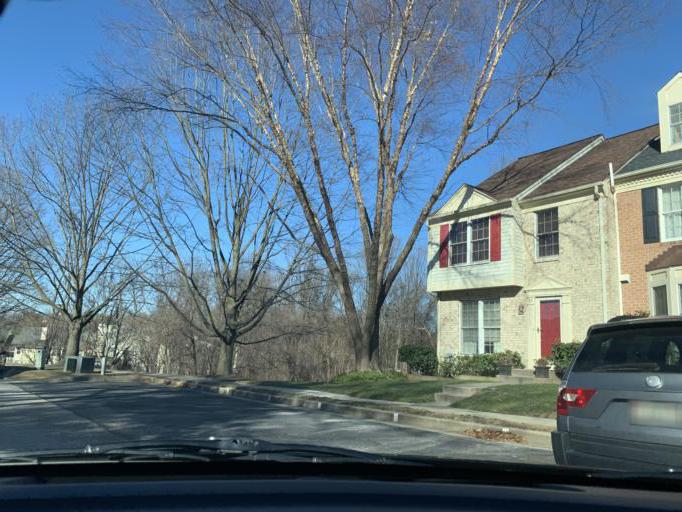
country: US
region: Maryland
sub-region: Baltimore County
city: Garrison
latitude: 39.3980
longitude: -76.7556
